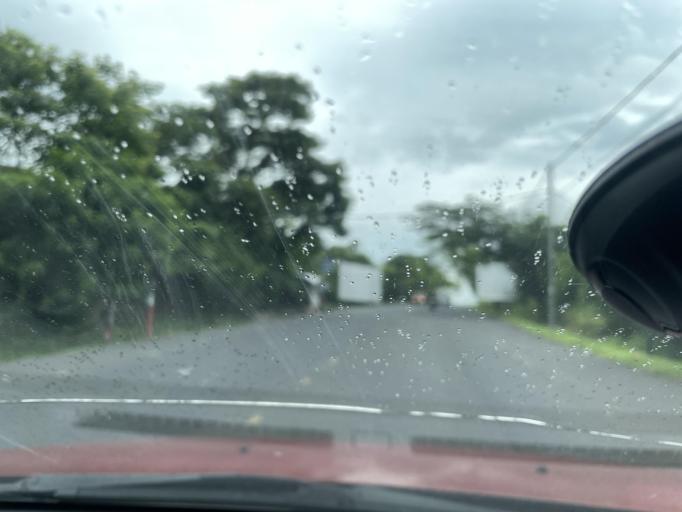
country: SV
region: San Miguel
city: Chirilagua
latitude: 13.3327
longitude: -88.1472
